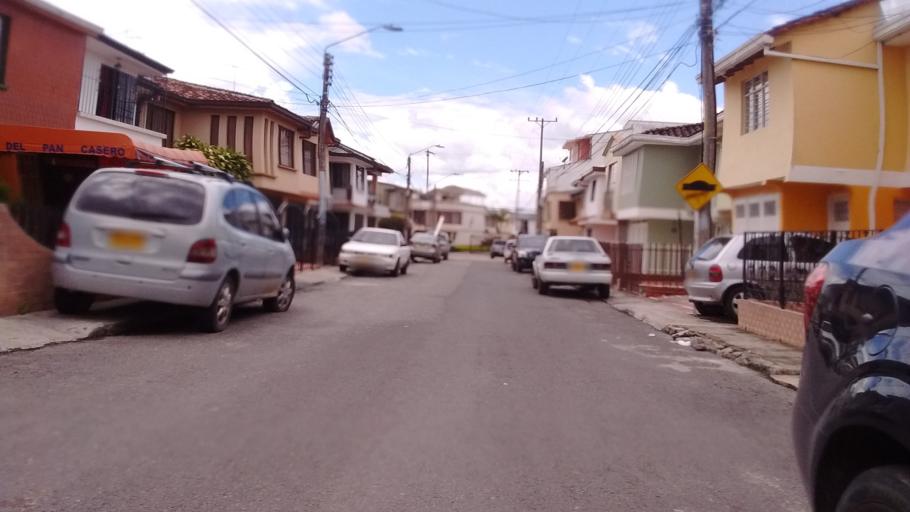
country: CO
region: Cauca
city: Popayan
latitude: 2.4602
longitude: -76.5872
